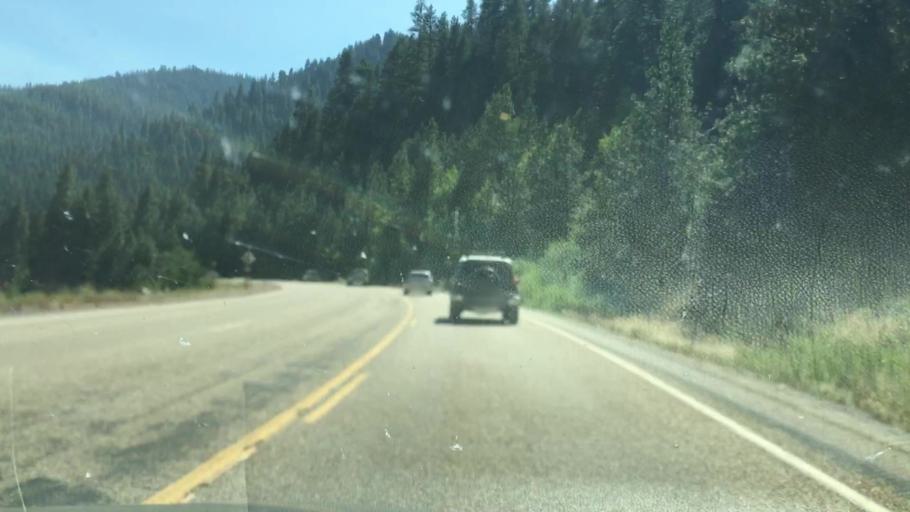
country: US
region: Idaho
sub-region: Valley County
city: Cascade
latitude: 44.1762
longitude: -116.1188
